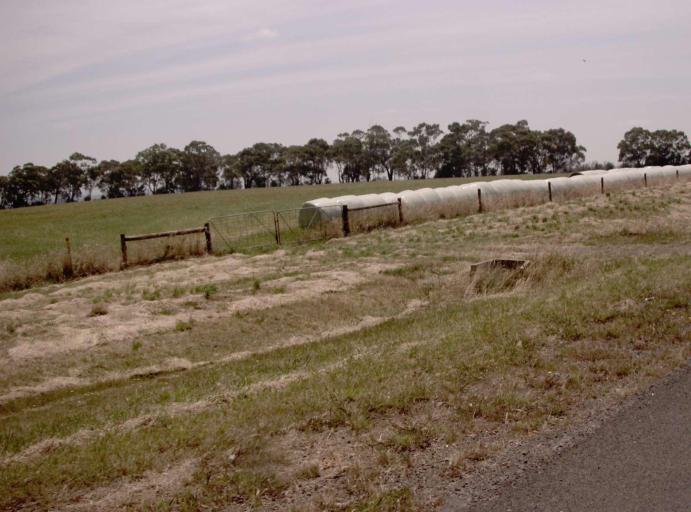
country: AU
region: Victoria
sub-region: Latrobe
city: Traralgon
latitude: -38.2430
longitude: 146.6276
